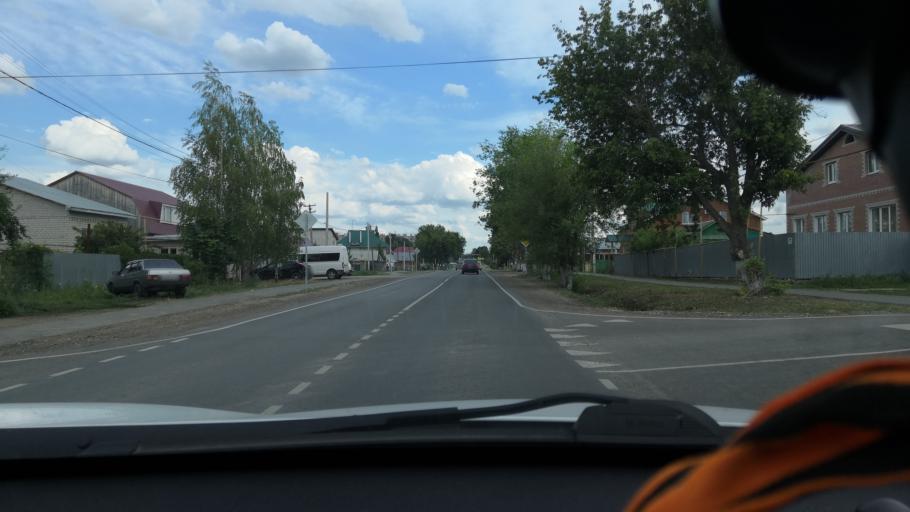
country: RU
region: Samara
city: Novosemeykino
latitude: 53.3748
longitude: 50.3479
